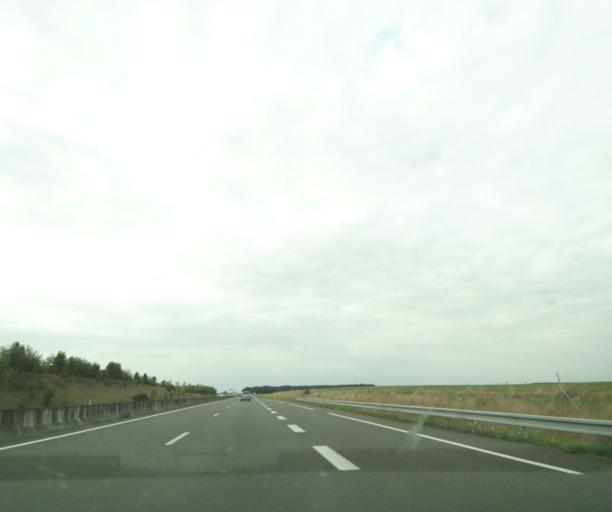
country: FR
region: Centre
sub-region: Departement d'Indre-et-Loire
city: Rouziers-de-Touraine
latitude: 47.5392
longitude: 0.6158
